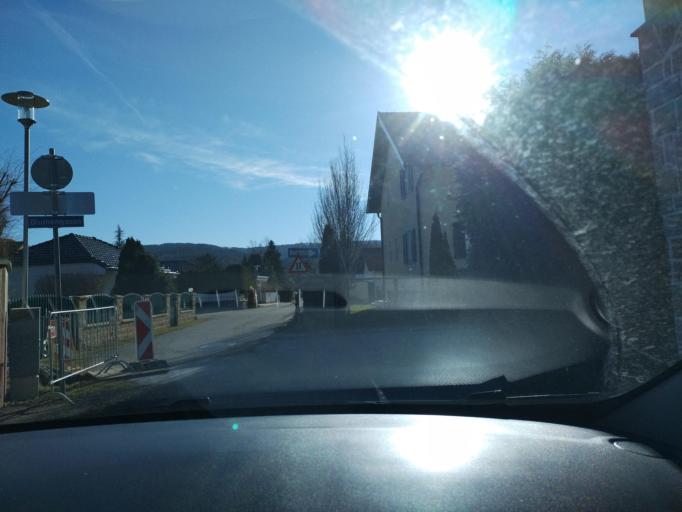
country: AT
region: Lower Austria
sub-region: Politischer Bezirk Wiener Neustadt
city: Lanzenkirchen
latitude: 47.7520
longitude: 16.2508
